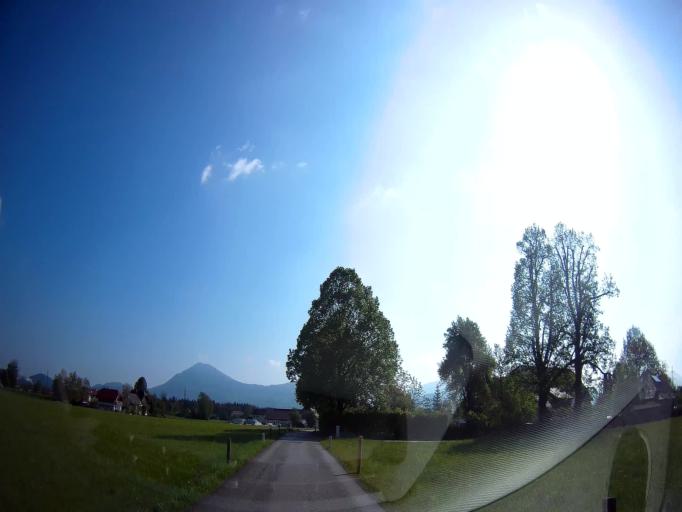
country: AT
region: Salzburg
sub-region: Politischer Bezirk Salzburg-Umgebung
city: Grodig
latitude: 47.7521
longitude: 13.0273
